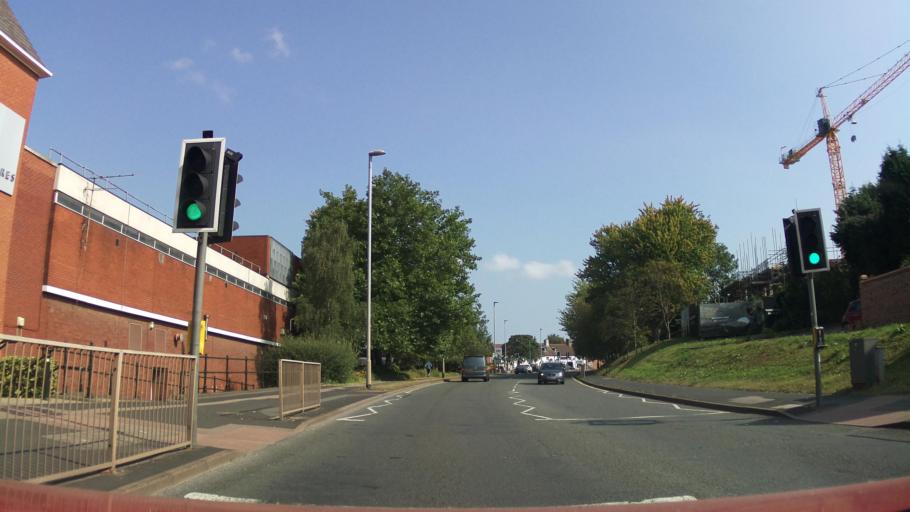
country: GB
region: England
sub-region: Staffordshire
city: Lichfield
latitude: 52.6824
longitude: -1.8241
